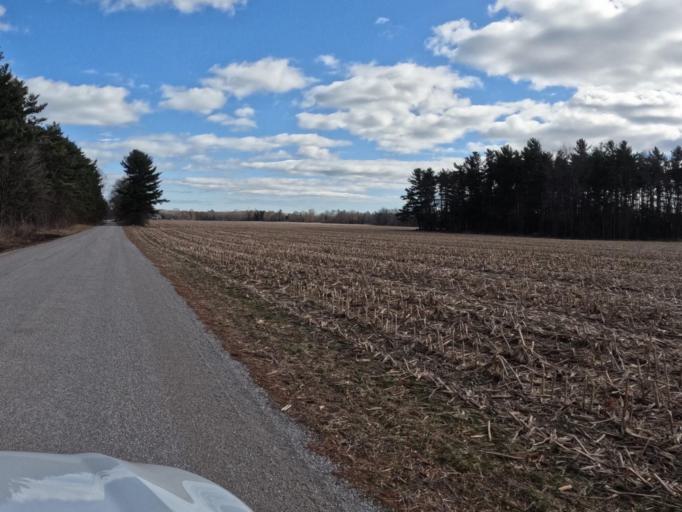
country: CA
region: Ontario
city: Norfolk County
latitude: 42.7512
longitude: -80.3003
